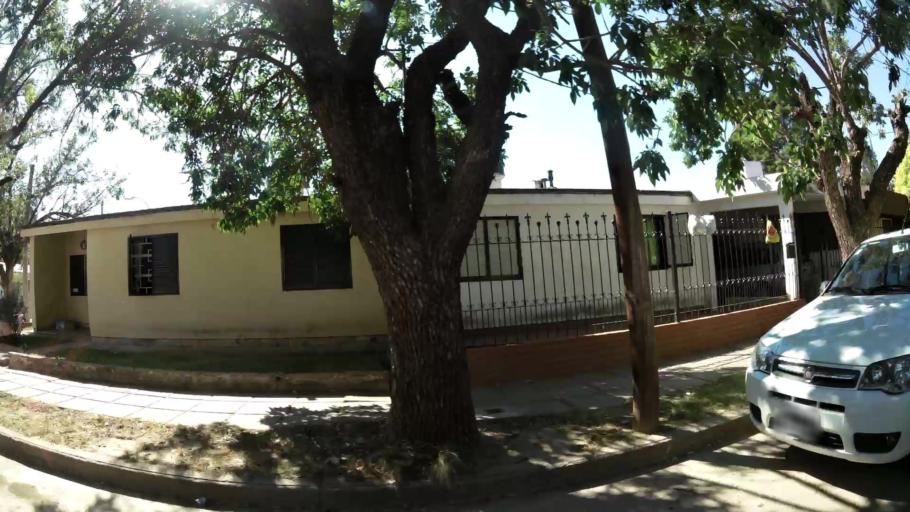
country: AR
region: Cordoba
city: Villa Allende
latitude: -31.3410
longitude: -64.2400
